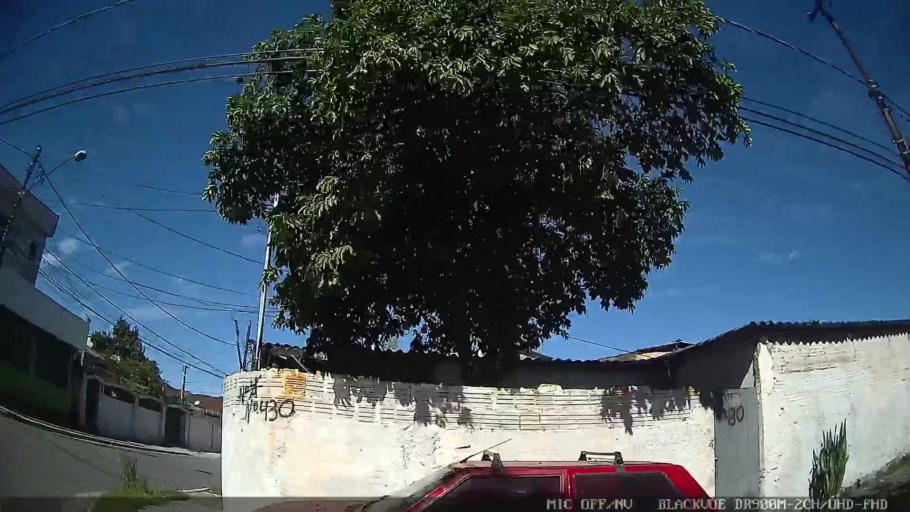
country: BR
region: Sao Paulo
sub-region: Santos
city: Santos
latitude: -23.9476
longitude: -46.2943
